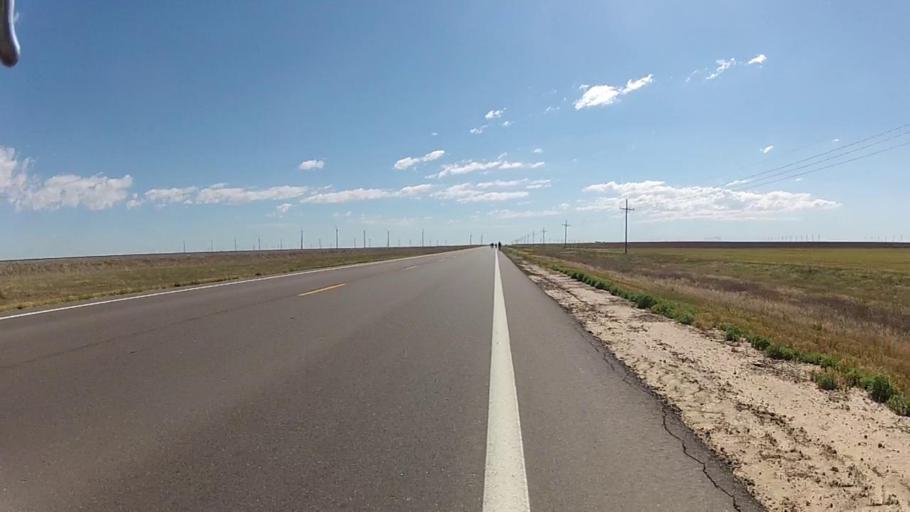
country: US
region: Kansas
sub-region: Gray County
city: Cimarron
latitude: 37.6038
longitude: -100.4263
